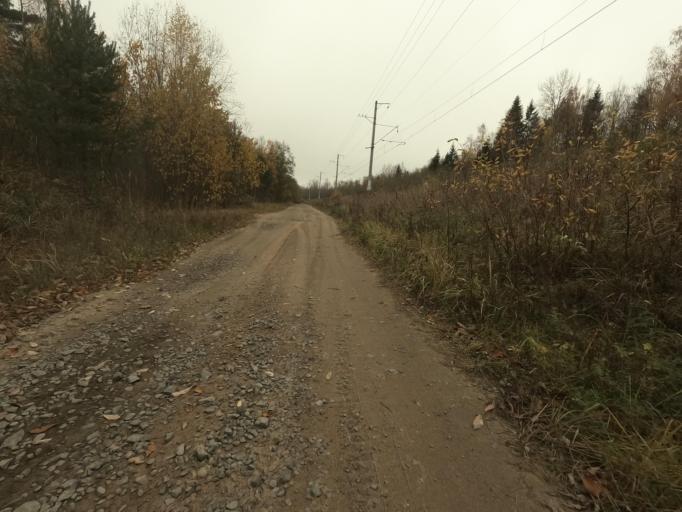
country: RU
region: Leningrad
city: Pavlovo
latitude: 59.7821
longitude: 30.8957
